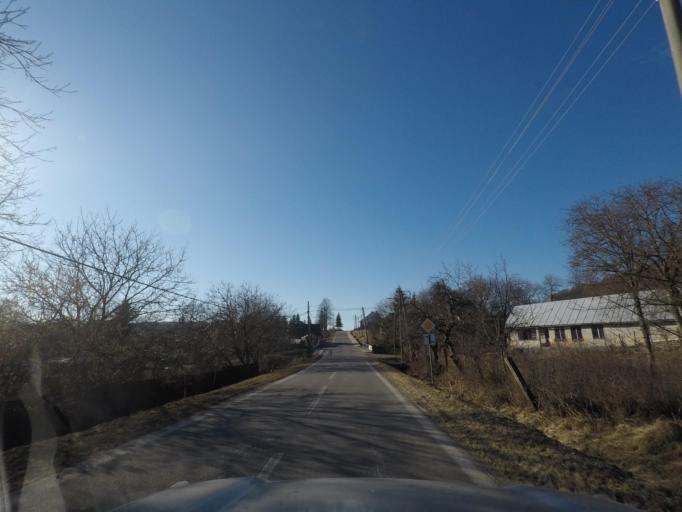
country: SK
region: Presovsky
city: Medzilaborce
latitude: 49.2221
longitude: 21.9752
